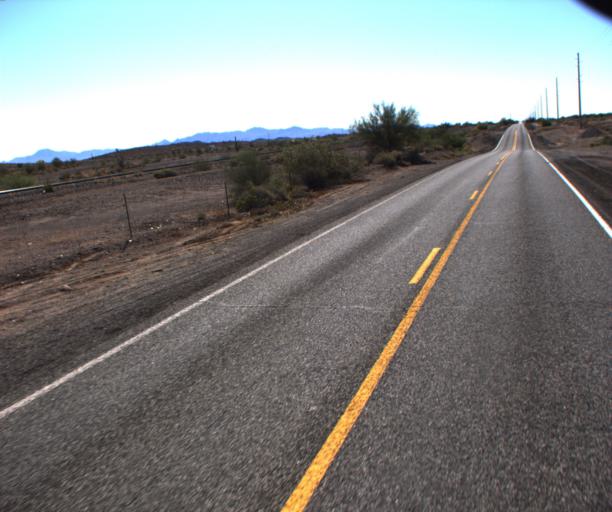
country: US
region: Arizona
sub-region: La Paz County
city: Quartzsite
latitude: 33.9081
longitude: -113.9838
